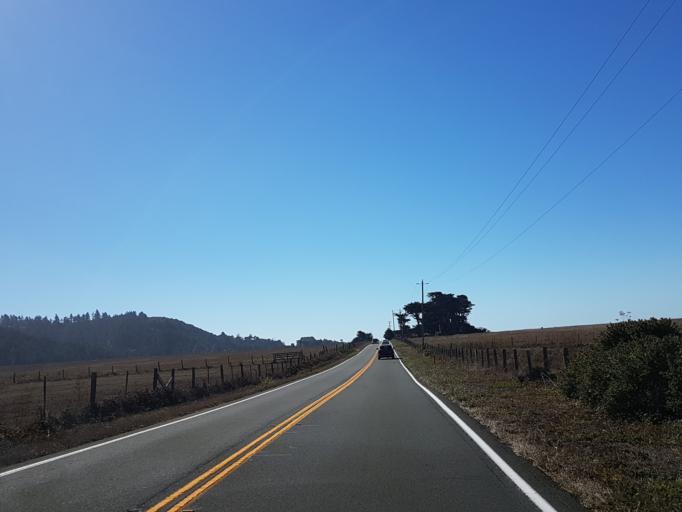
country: US
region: California
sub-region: Mendocino County
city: Boonville
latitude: 39.0458
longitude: -123.6852
